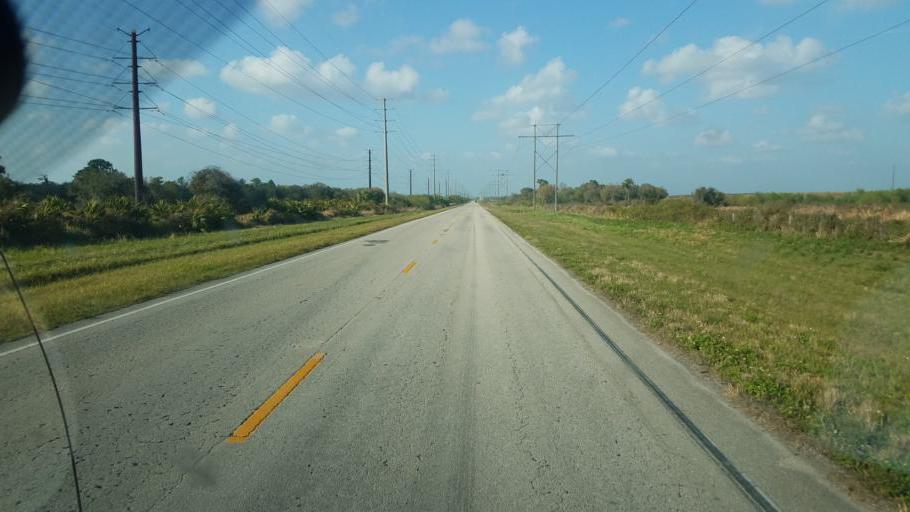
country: US
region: Florida
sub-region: Hardee County
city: Wauchula
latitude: 27.5550
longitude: -81.9324
